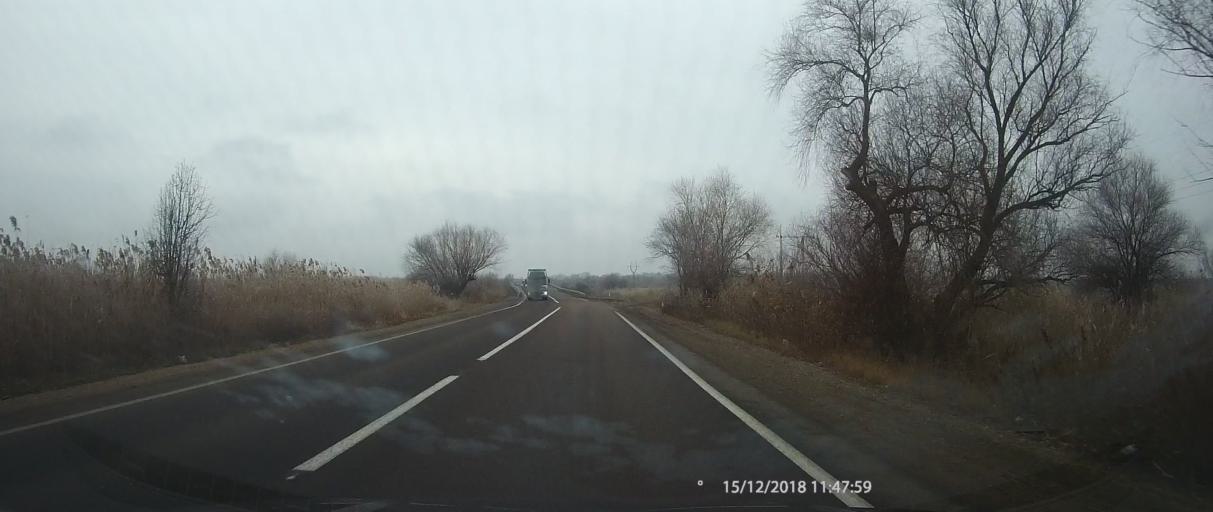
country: UA
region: Odessa
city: Bilyayivka
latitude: 46.4137
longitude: 30.1591
